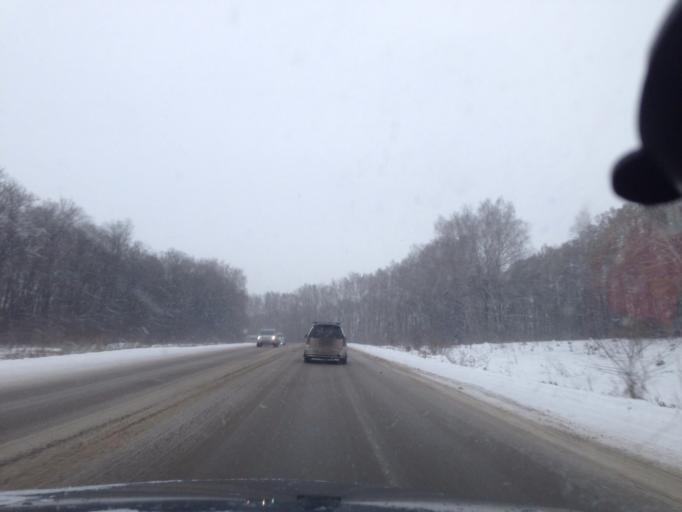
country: RU
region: Tula
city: Skuratovskiy
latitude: 54.1284
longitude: 37.6816
